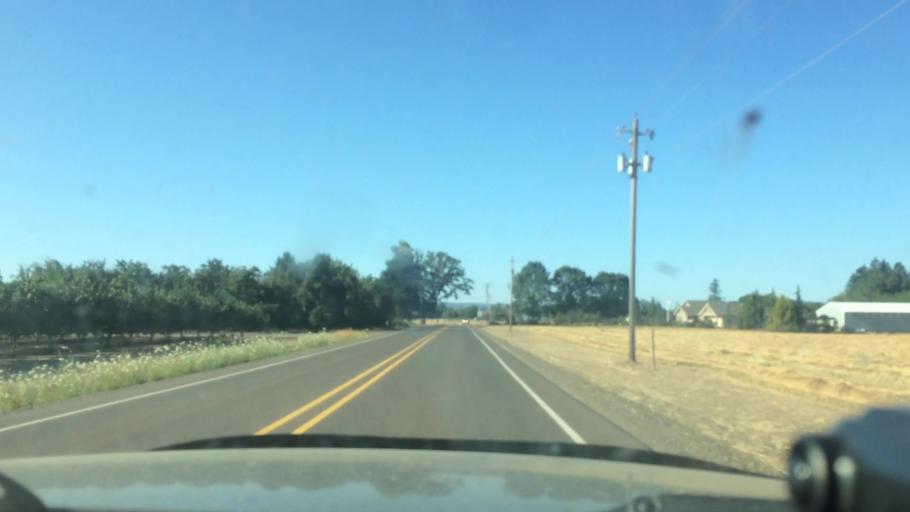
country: US
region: Oregon
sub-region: Yamhill County
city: Dundee
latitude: 45.1998
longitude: -122.9834
